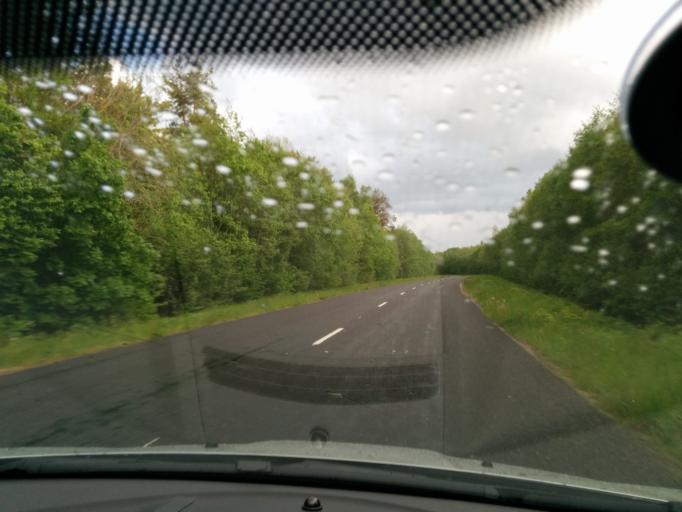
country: EE
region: Harju
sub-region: Loksa linn
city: Loksa
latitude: 59.6378
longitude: 25.7581
